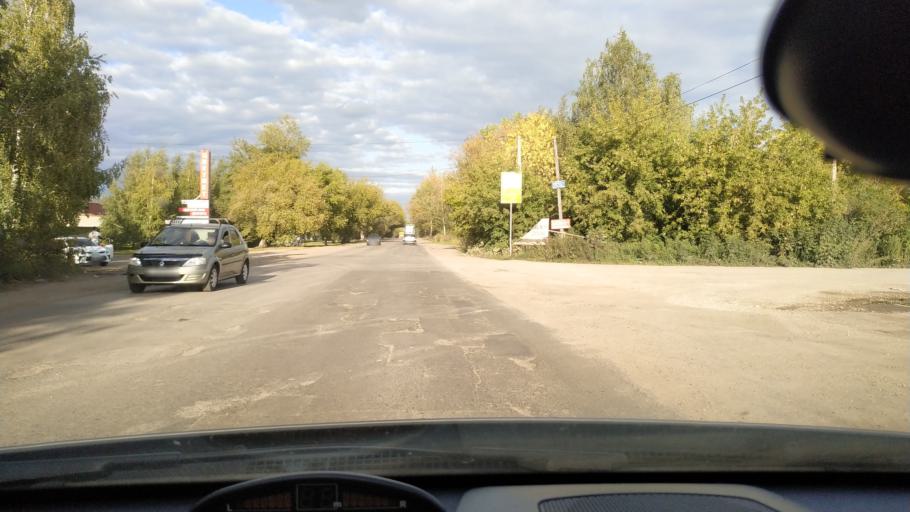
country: RU
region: Rjazan
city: Polyany
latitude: 54.5811
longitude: 39.8236
